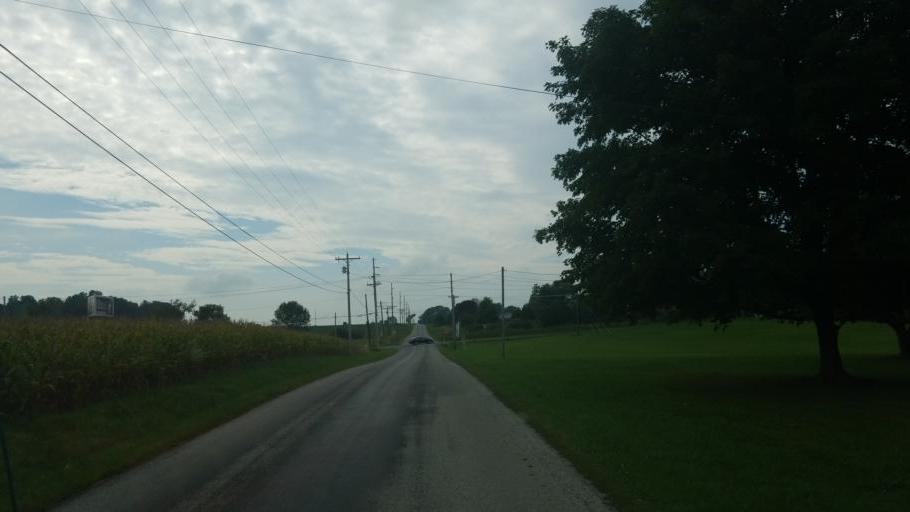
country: US
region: Ohio
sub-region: Wayne County
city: Wooster
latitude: 40.9011
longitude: -81.9743
